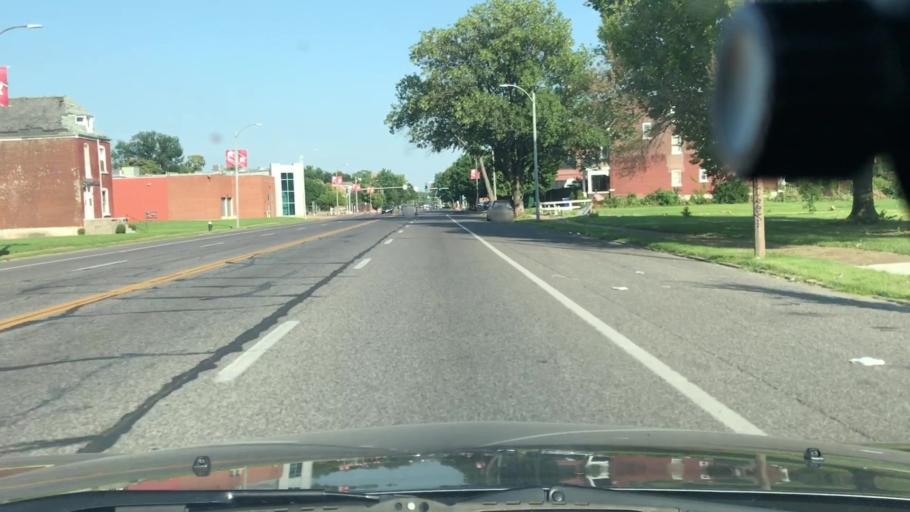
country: US
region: Missouri
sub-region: Saint Louis County
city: Hillsdale
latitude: 38.6553
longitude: -90.2488
